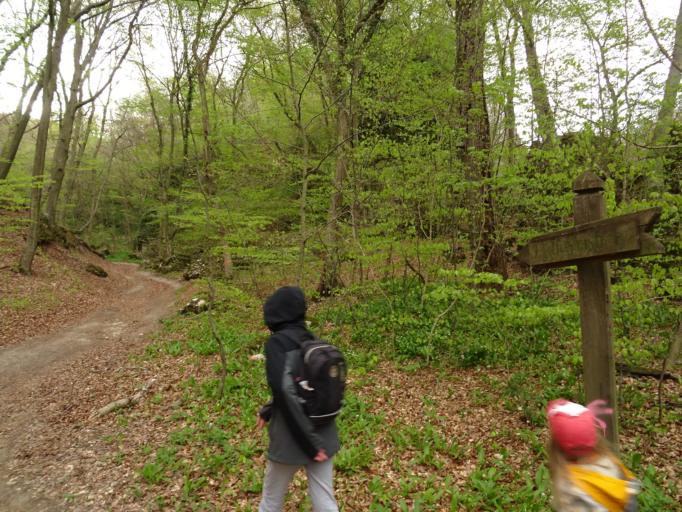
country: HU
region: Veszprem
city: Varpalota
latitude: 47.2280
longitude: 18.0986
